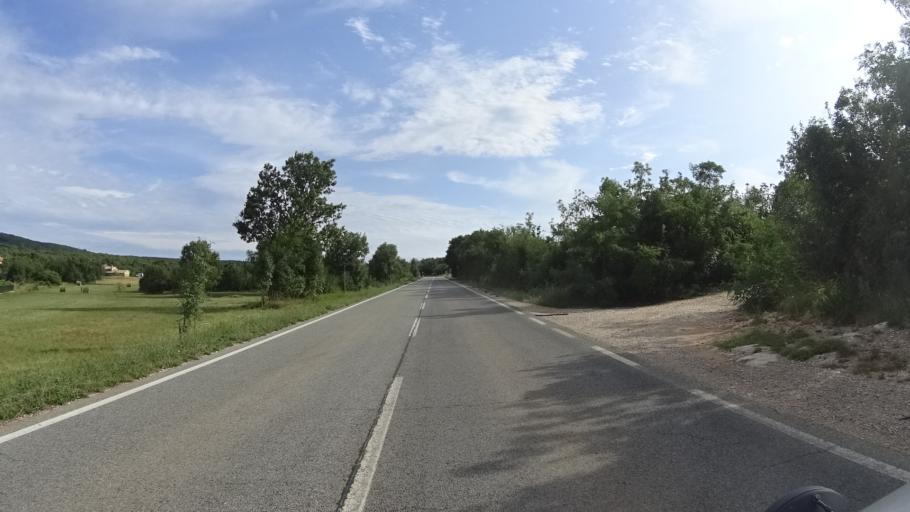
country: HR
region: Istarska
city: Rasa
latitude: 45.0670
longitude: 14.0912
